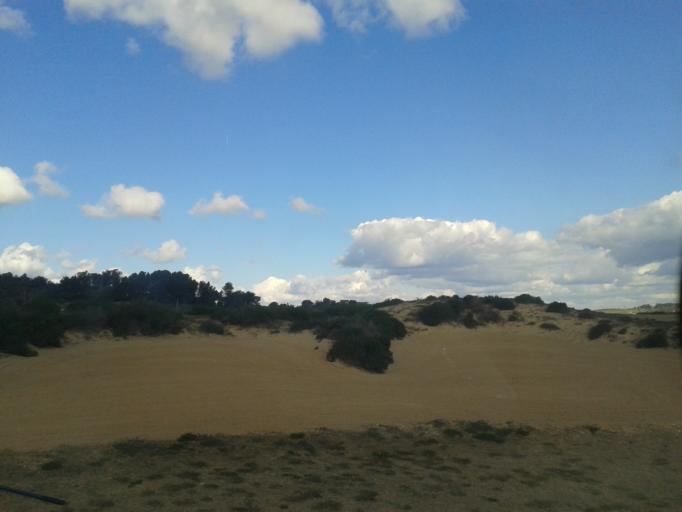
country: PT
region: Faro
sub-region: Lagos
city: Lagos
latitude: 37.1204
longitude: -8.6398
